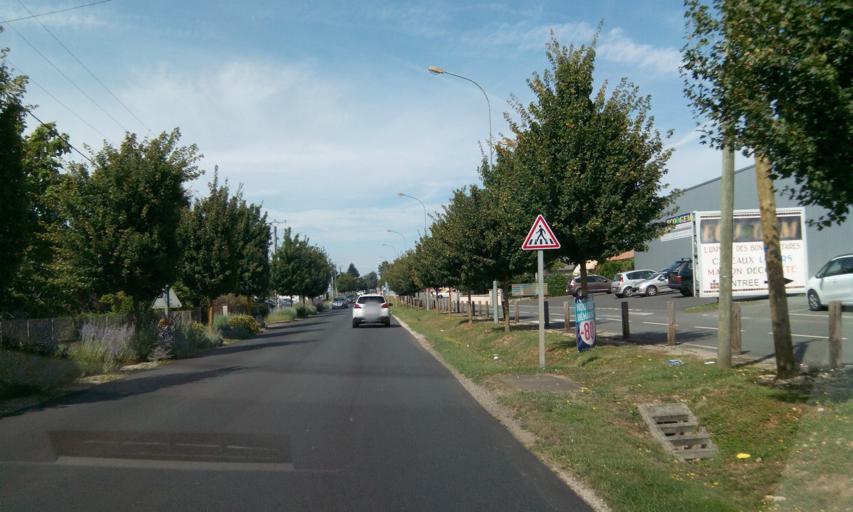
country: FR
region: Poitou-Charentes
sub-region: Departement de la Vienne
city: Savigne
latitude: 46.1597
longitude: 0.3091
